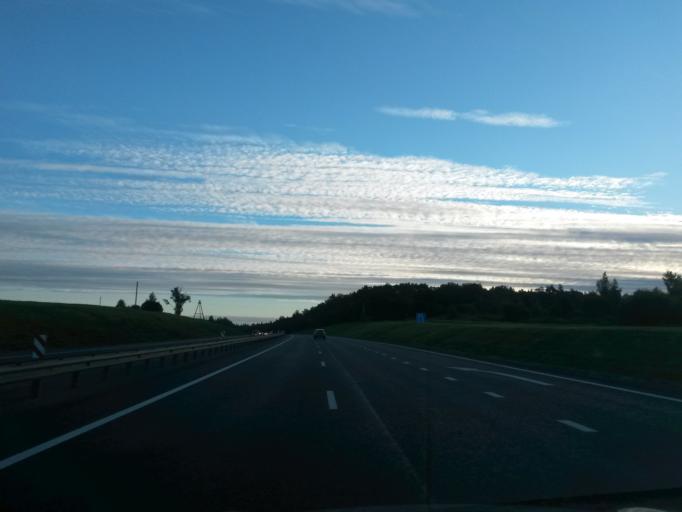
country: RU
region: Moskovskaya
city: Krasnozavodsk
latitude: 56.4286
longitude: 38.3411
